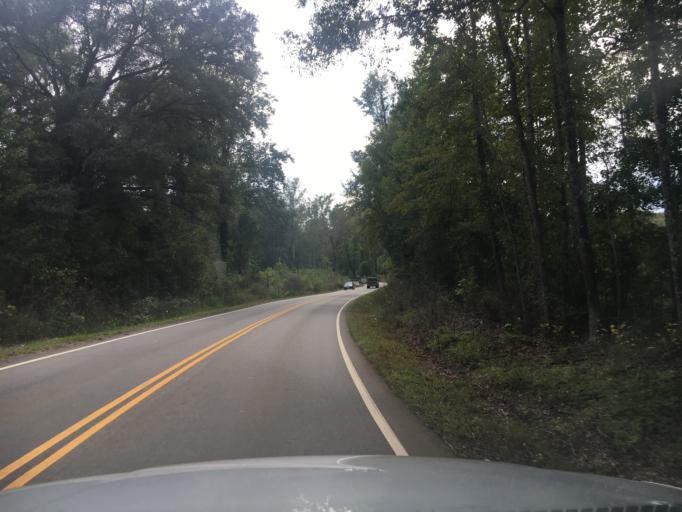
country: US
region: South Carolina
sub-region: Spartanburg County
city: Wellford
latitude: 34.9269
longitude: -82.0610
